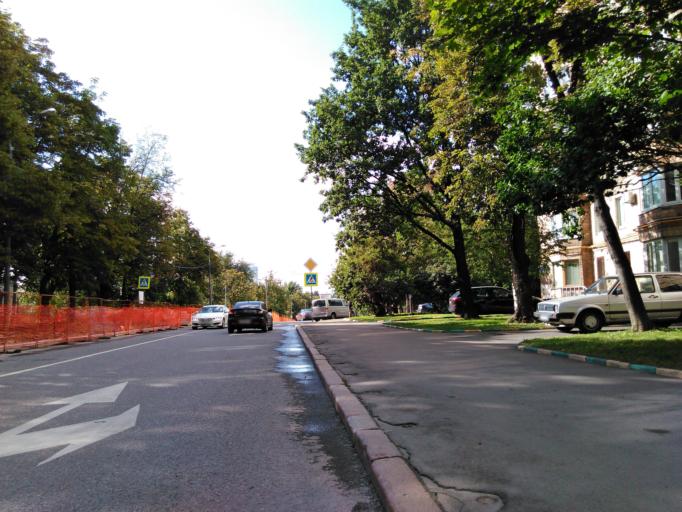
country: RU
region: Moscow
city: Luzhniki
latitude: 55.7280
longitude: 37.5599
